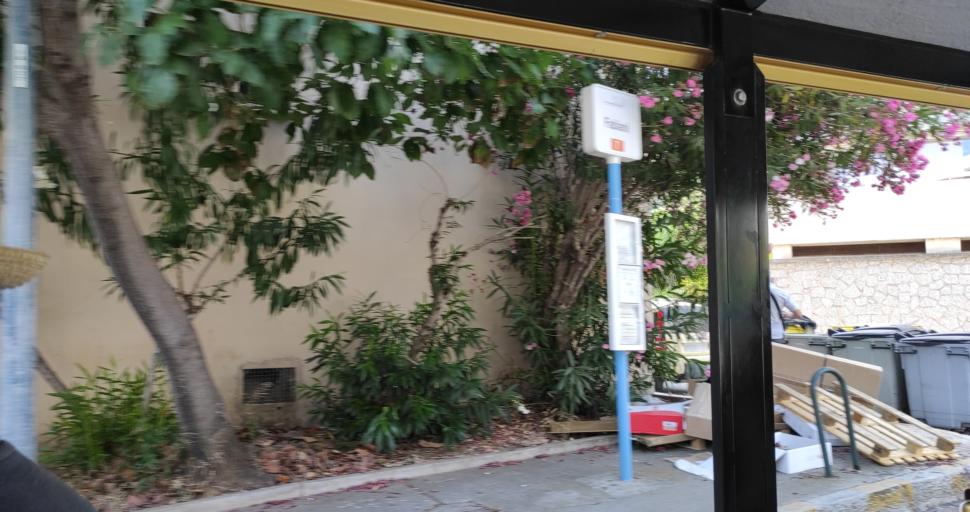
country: FR
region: Corsica
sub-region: Departement de la Corse-du-Sud
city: Ajaccio
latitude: 41.9163
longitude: 8.7264
